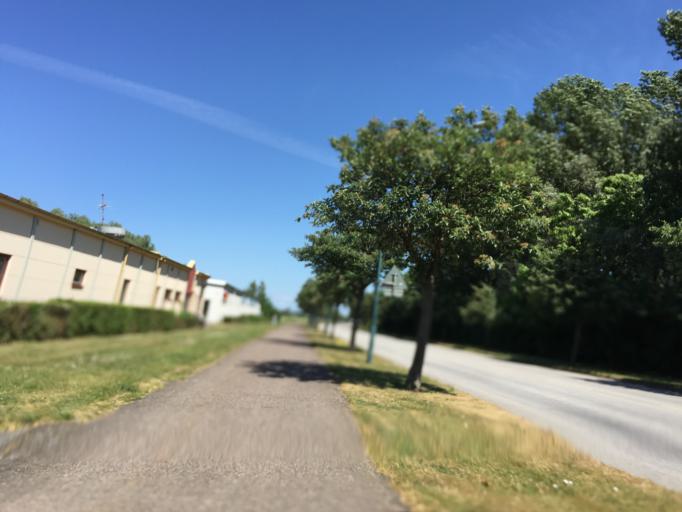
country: SE
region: Skane
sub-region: Trelleborgs Kommun
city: Trelleborg
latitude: 55.3799
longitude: 13.1240
